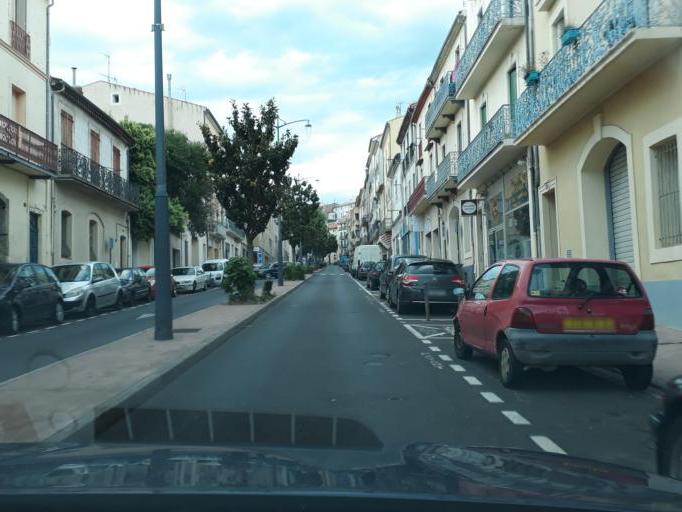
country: FR
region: Languedoc-Roussillon
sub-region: Departement de l'Herault
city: Beziers
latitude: 43.3381
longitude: 3.2181
